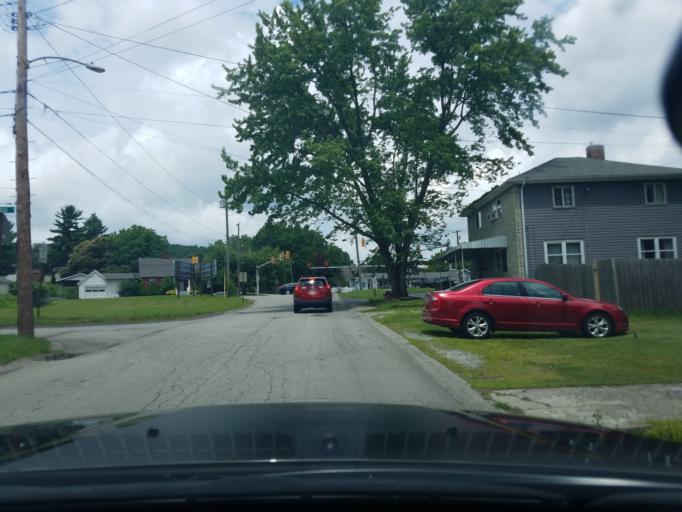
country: US
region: Pennsylvania
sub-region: Westmoreland County
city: Youngwood
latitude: 40.2298
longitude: -79.5865
